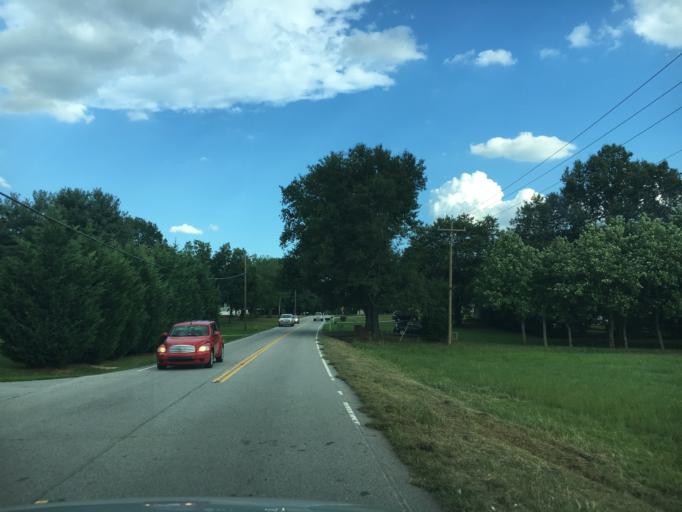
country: US
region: South Carolina
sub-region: Greenville County
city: Greer
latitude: 34.9097
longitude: -82.2341
